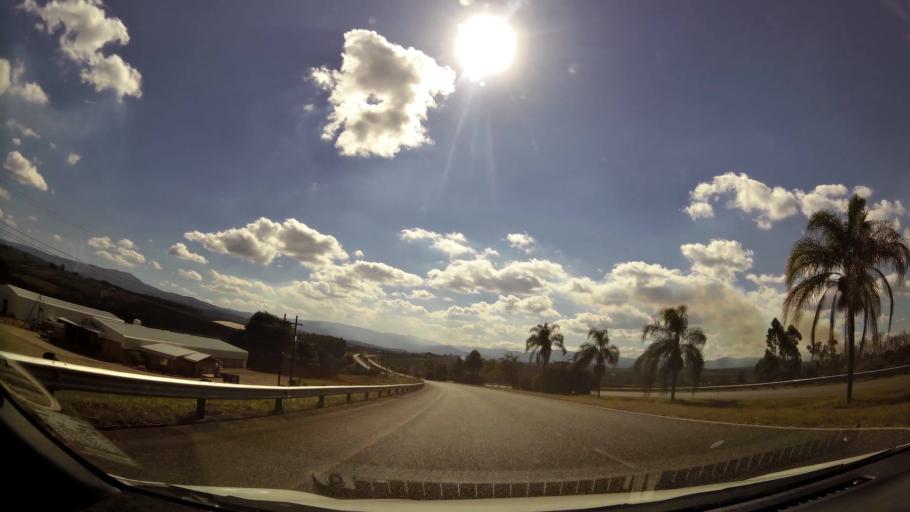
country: ZA
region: Limpopo
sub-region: Mopani District Municipality
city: Tzaneen
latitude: -23.8303
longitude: 30.1343
